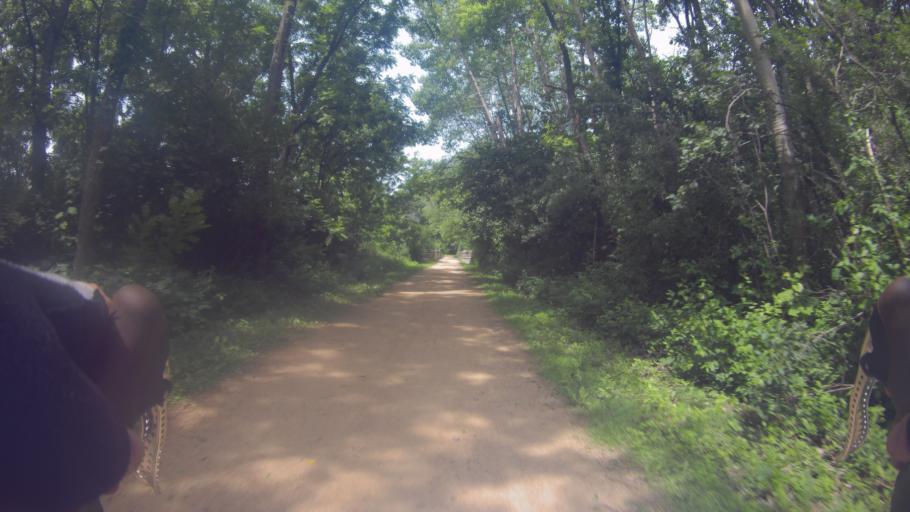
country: US
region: Wisconsin
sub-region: Dane County
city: Mount Horeb
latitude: 43.0149
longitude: -89.7008
